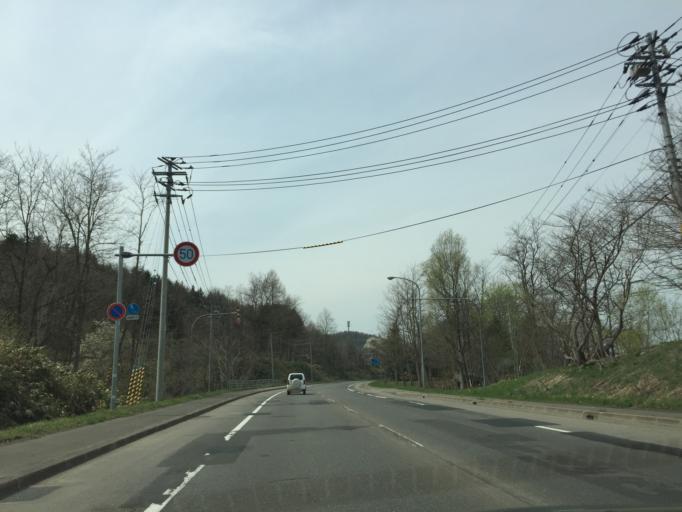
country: JP
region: Hokkaido
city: Akabira
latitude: 43.5395
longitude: 142.0728
